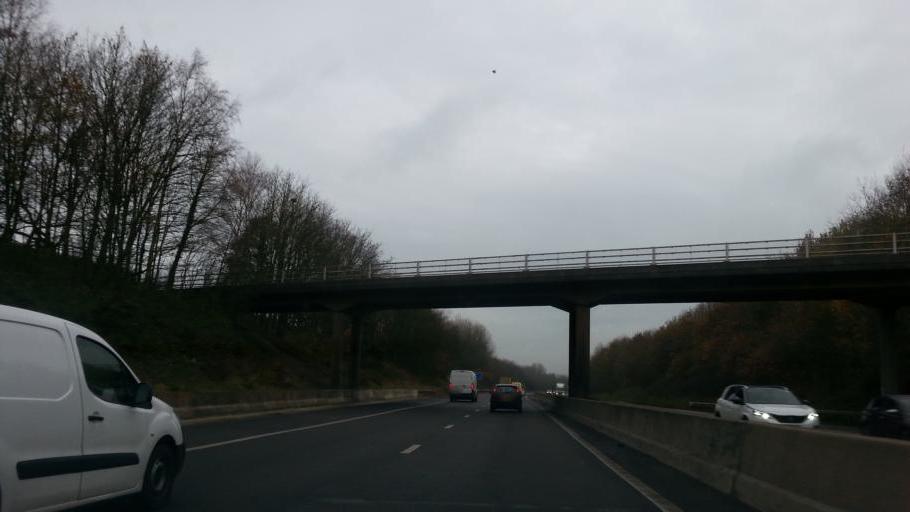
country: GB
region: England
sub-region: Shropshire
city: Shifnal
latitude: 52.6761
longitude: -2.3566
